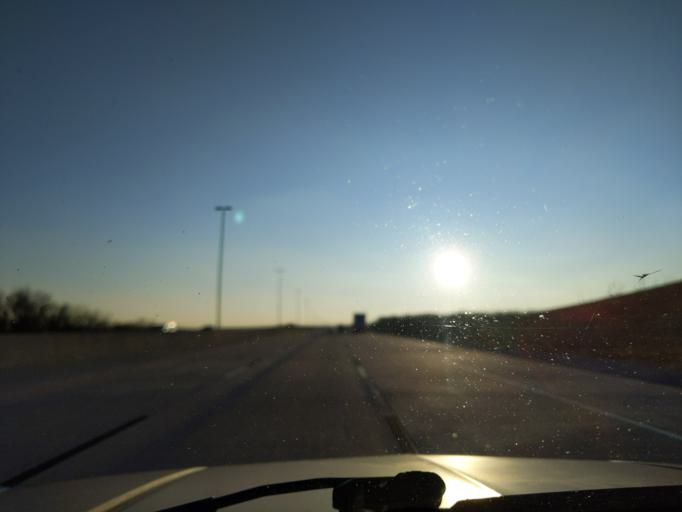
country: US
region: Oklahoma
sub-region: Creek County
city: Kellyville
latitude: 35.9553
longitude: -96.2385
